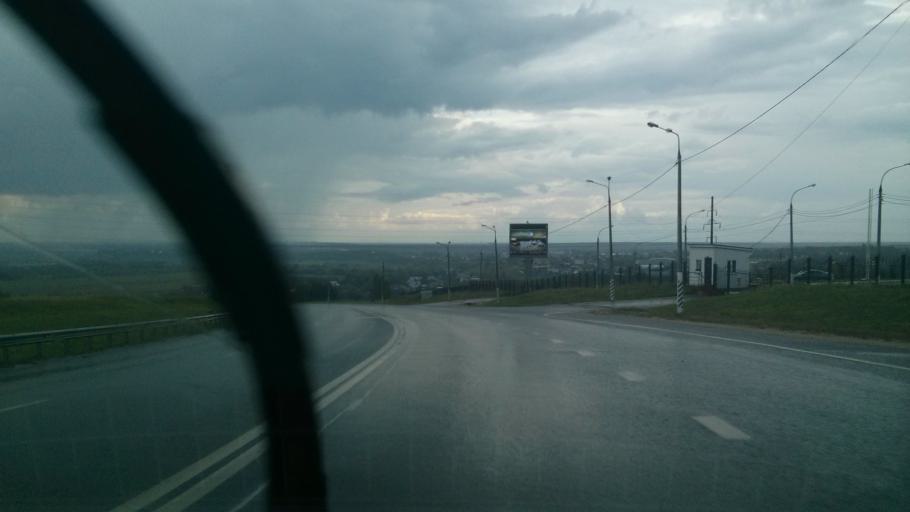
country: RU
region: Nizjnij Novgorod
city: Afonino
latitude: 56.2448
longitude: 44.1002
